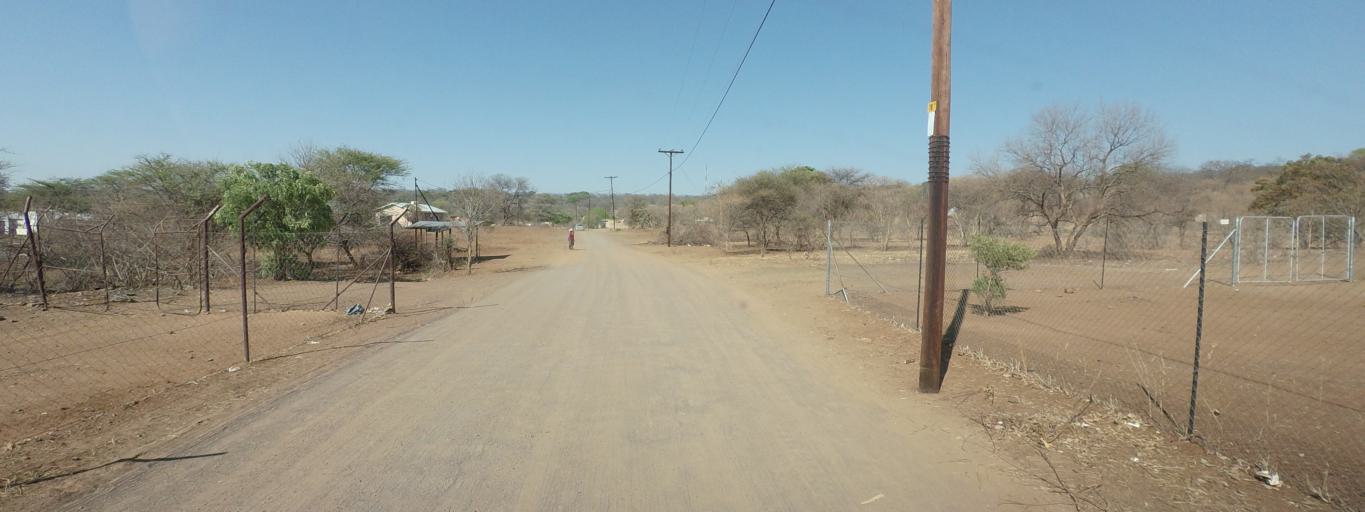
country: BW
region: North West
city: Kasane
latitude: -17.8991
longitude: 25.2239
